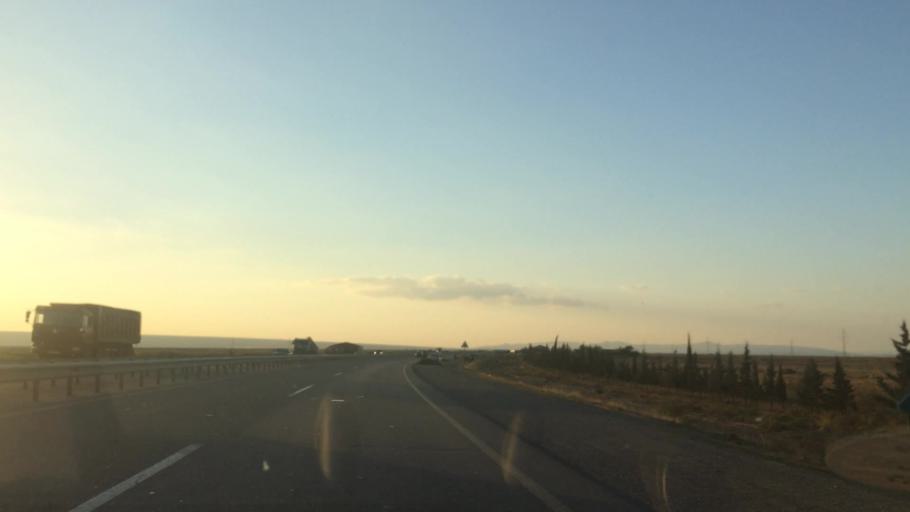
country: AZ
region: Baki
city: Qobustan
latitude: 39.9832
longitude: 49.2161
